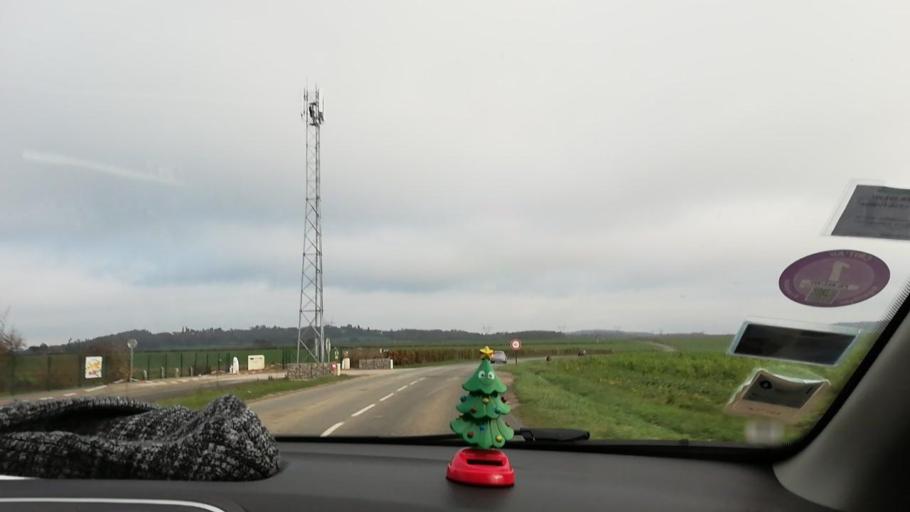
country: FR
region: Ile-de-France
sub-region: Departement de Seine-et-Marne
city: Monthyon
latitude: 48.9997
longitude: 2.7974
